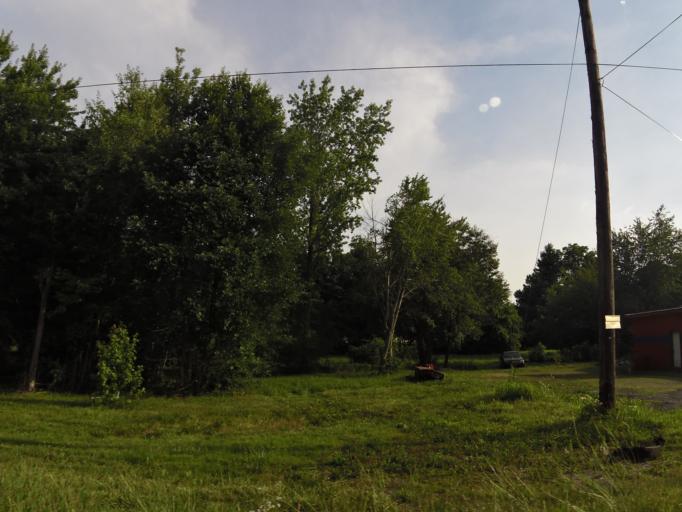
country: US
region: Tennessee
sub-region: Humphreys County
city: McEwen
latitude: 36.1057
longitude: -87.6269
